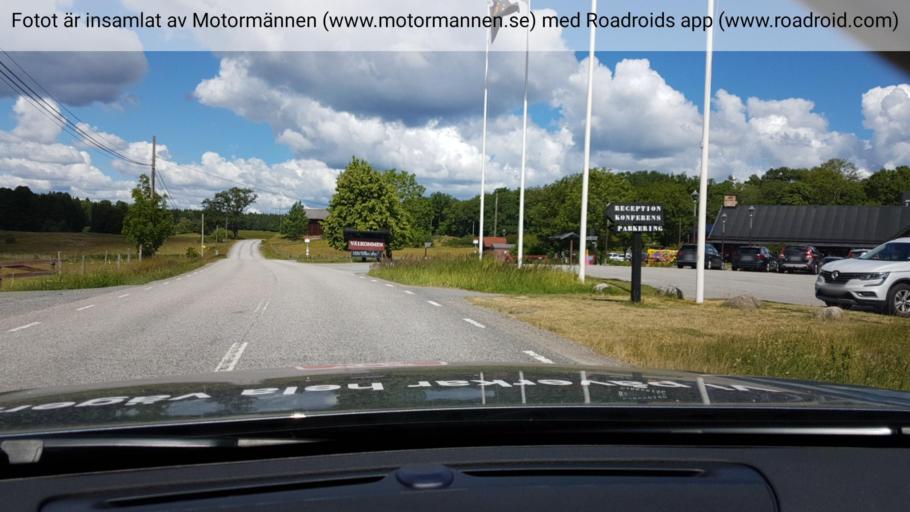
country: SE
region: Stockholm
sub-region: Varmdo Kommun
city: Hemmesta
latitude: 59.3716
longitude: 18.5285
